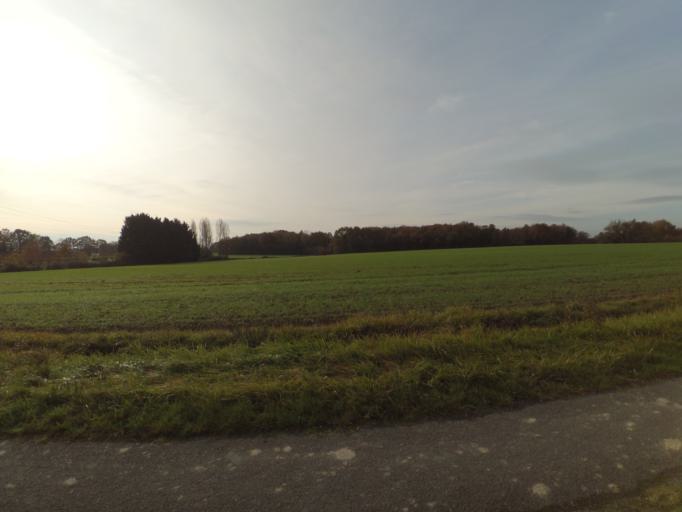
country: FR
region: Pays de la Loire
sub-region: Departement de la Loire-Atlantique
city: La Planche
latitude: 47.0041
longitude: -1.3935
